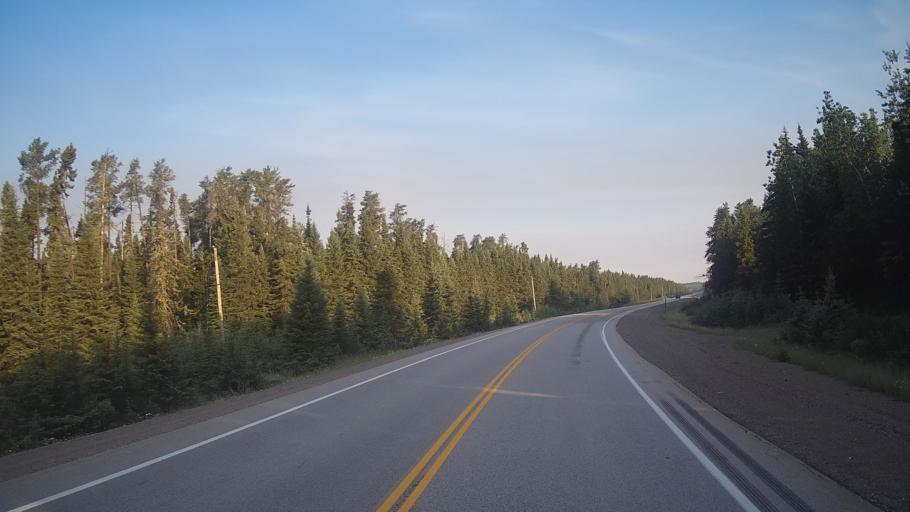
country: CA
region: Ontario
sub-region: Rainy River District
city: Atikokan
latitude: 49.2417
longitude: -91.0854
